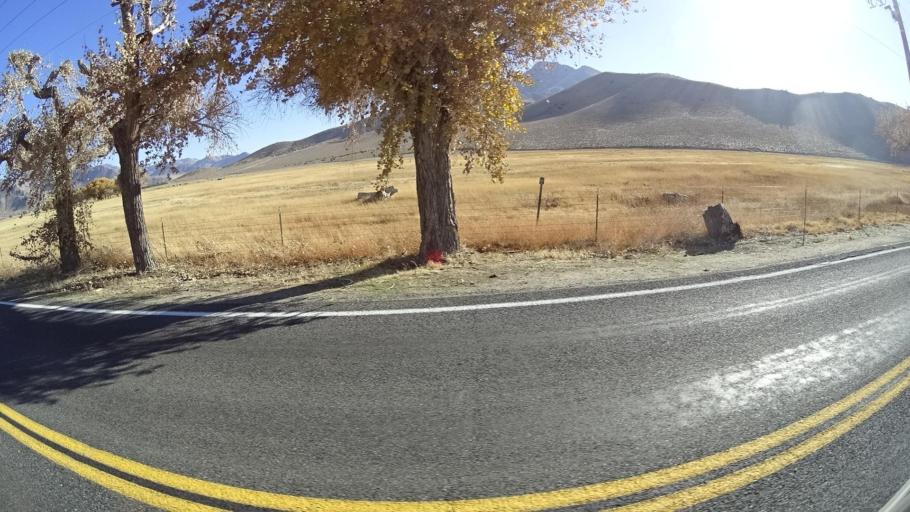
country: US
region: California
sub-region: Kern County
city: Weldon
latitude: 35.6655
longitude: -118.2931
